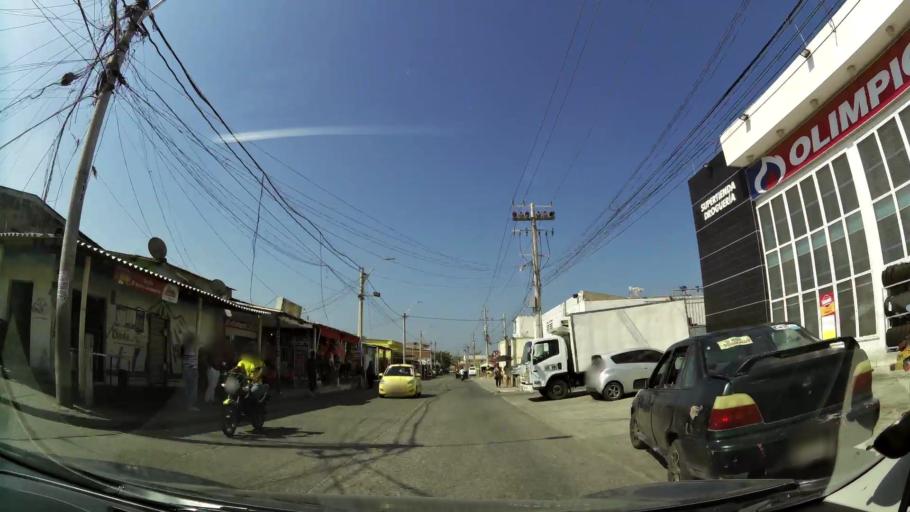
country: CO
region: Atlantico
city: Barranquilla
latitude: 10.9751
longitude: -74.8347
